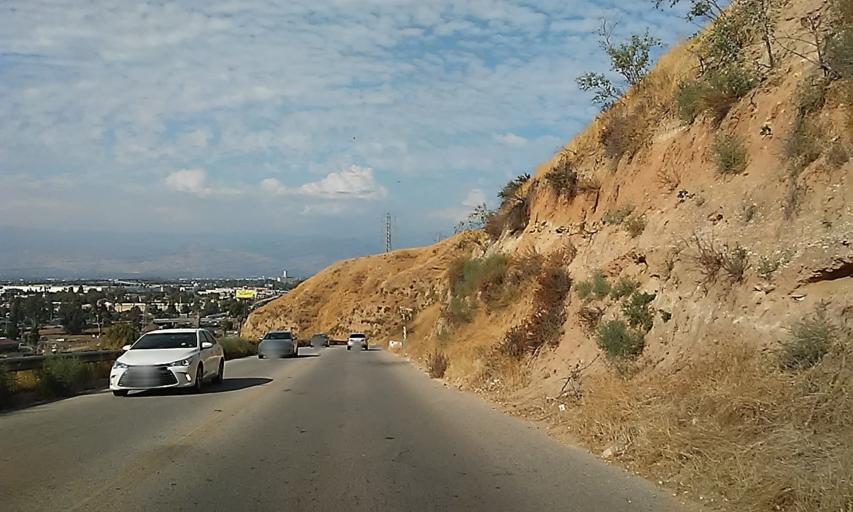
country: US
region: California
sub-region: San Bernardino County
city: Grand Terrace
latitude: 34.0431
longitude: -117.3116
